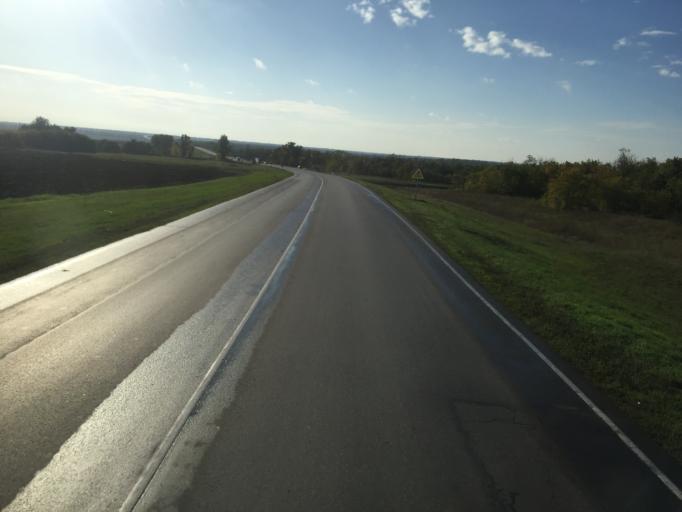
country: RU
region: Rostov
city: Mechetinskaya
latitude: 46.6756
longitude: 40.5271
